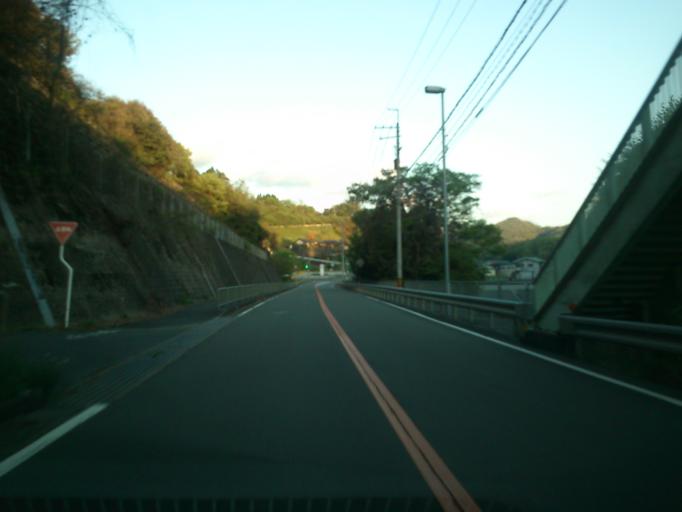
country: JP
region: Kyoto
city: Ayabe
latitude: 35.2149
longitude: 135.4224
